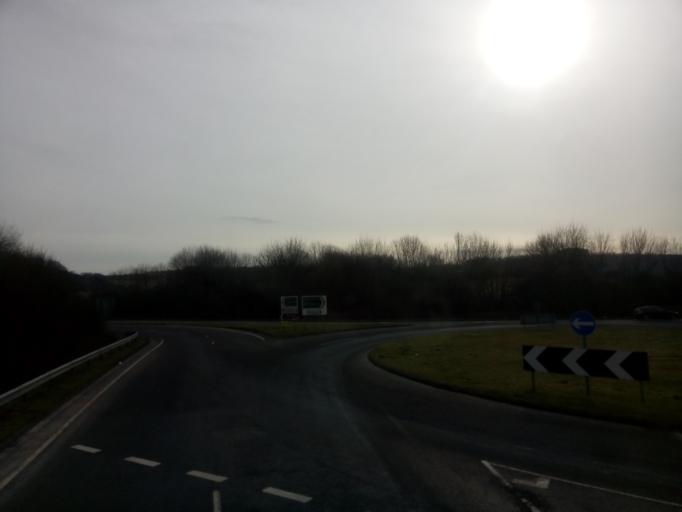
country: GB
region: England
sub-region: Hampshire
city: Winchester
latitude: 51.0598
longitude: -1.2925
